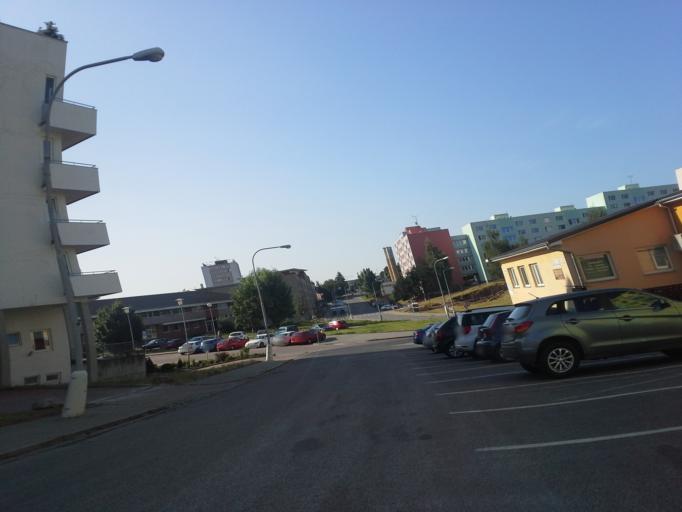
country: CZ
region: South Moravian
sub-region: Mesto Brno
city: Mokra Hora
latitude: 49.2388
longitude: 16.5834
